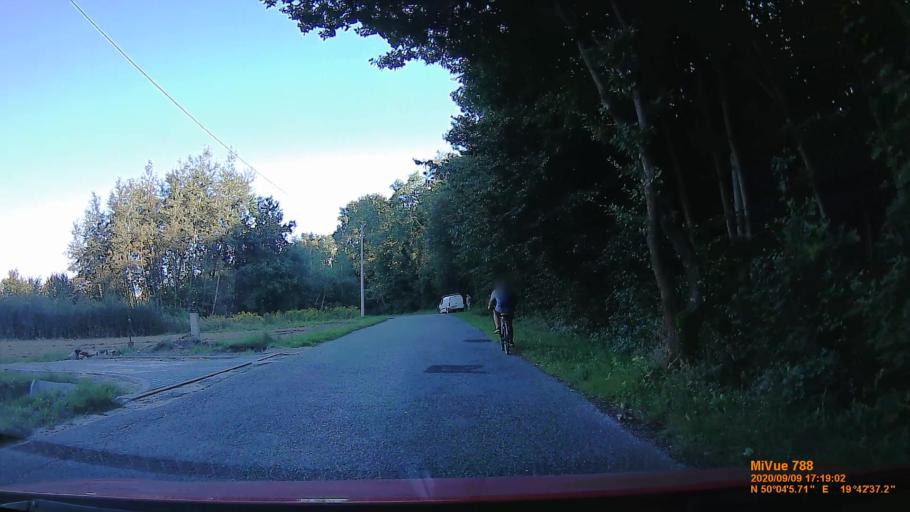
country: PL
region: Lesser Poland Voivodeship
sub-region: Powiat krakowski
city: Czulow
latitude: 50.0683
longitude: 19.7103
